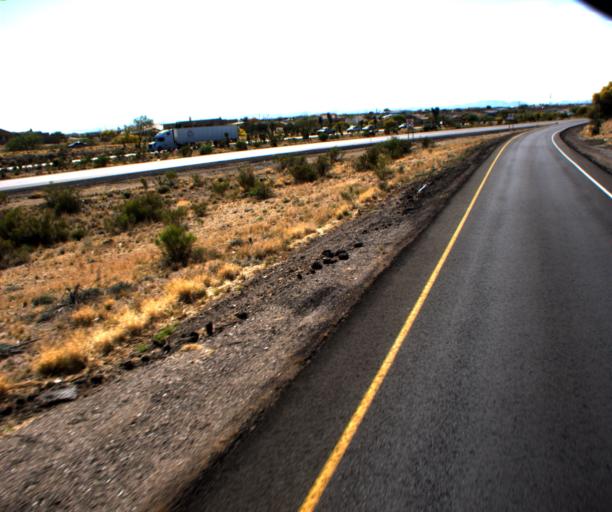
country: US
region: Arizona
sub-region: Pima County
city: Vail
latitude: 32.0098
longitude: -110.6932
